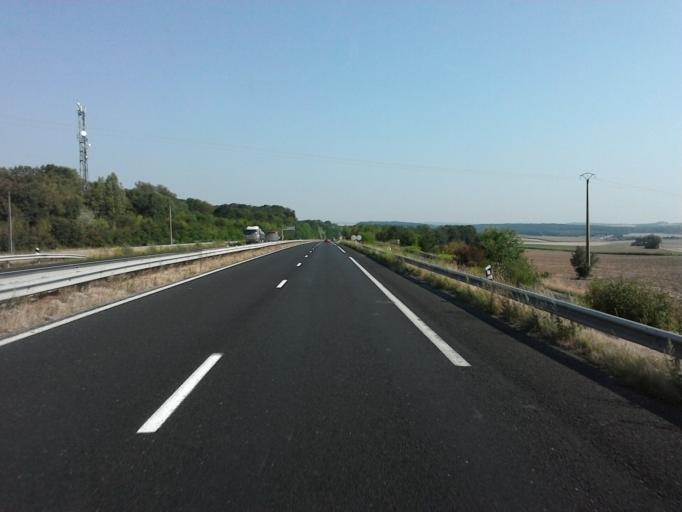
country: FR
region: Lorraine
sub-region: Departement des Vosges
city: Charmes
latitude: 48.4173
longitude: 6.2317
